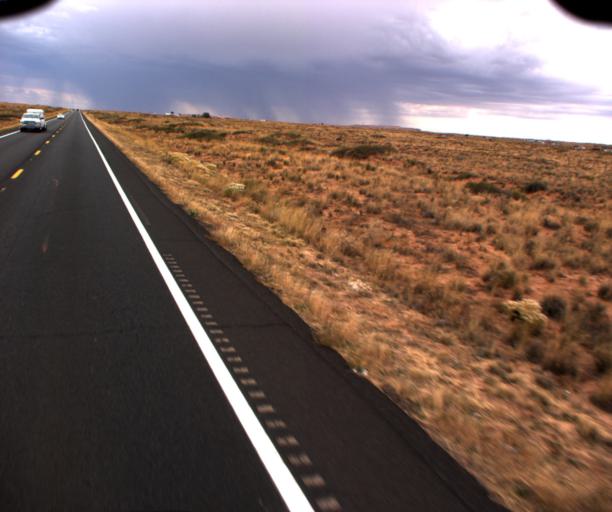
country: US
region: Arizona
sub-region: Coconino County
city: Kaibito
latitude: 36.3123
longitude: -110.9589
